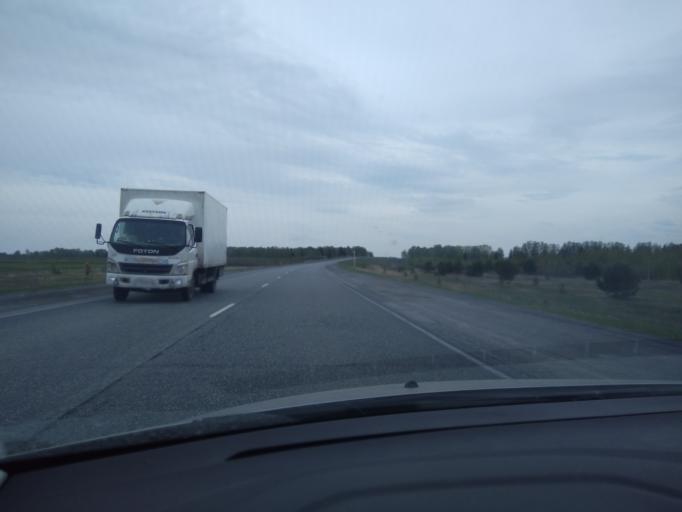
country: RU
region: Sverdlovsk
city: Kamyshlov
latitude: 56.8600
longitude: 62.7991
